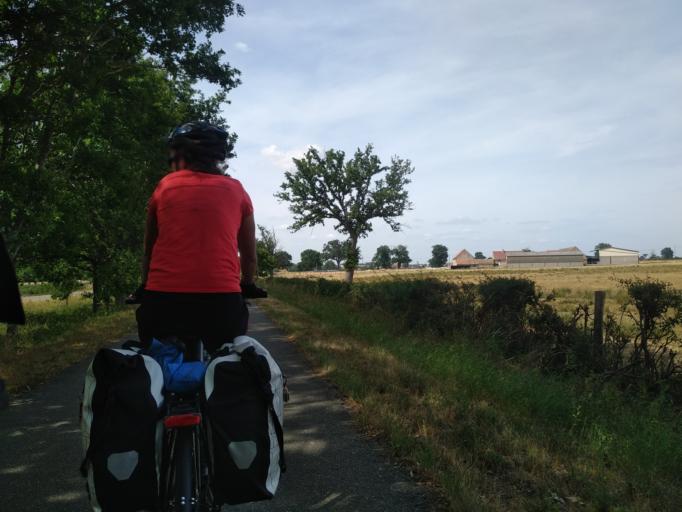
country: FR
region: Bourgogne
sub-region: Departement de Saone-et-Loire
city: Bourbon-Lancy
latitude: 46.6099
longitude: 3.7440
